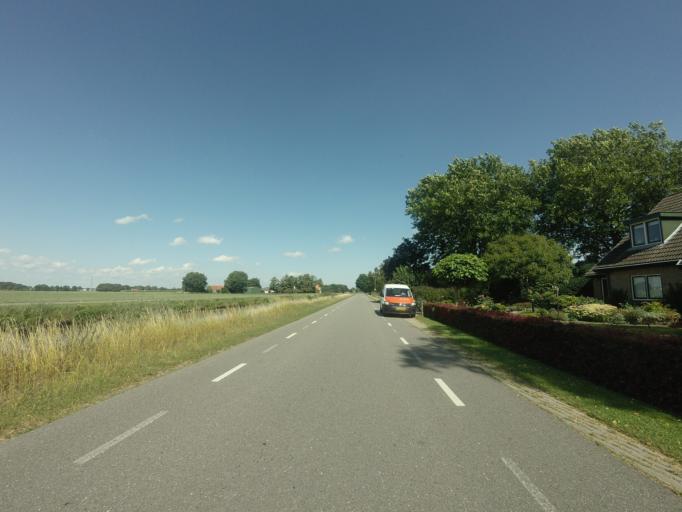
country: NL
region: Overijssel
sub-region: Gemeente Twenterand
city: Den Ham
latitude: 52.5675
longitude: 6.4388
